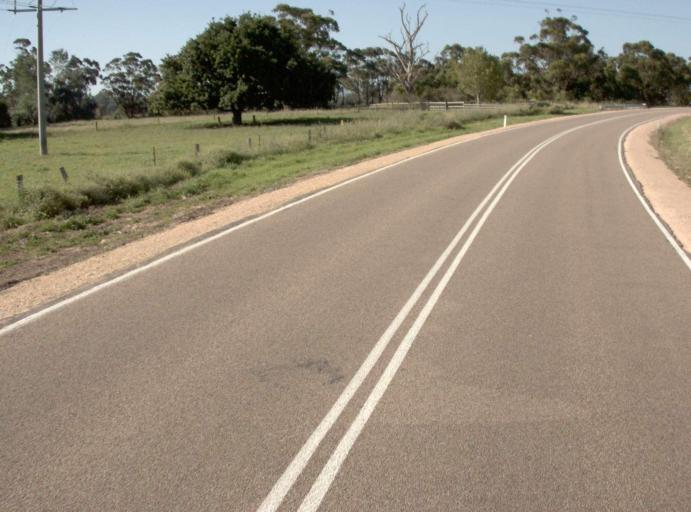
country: AU
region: Victoria
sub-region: East Gippsland
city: Lakes Entrance
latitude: -37.7696
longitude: 148.5367
